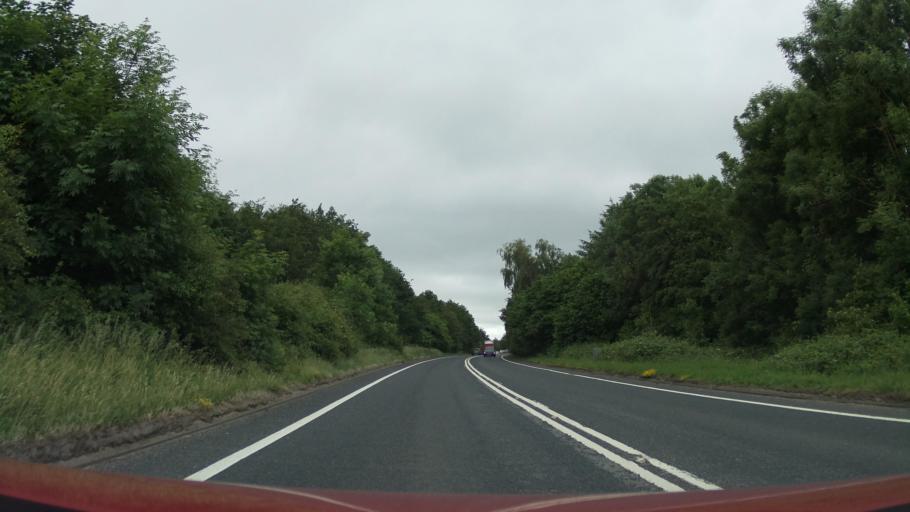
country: GB
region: England
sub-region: Leicestershire
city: Ashby de la Zouch
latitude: 52.7426
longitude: -1.4392
